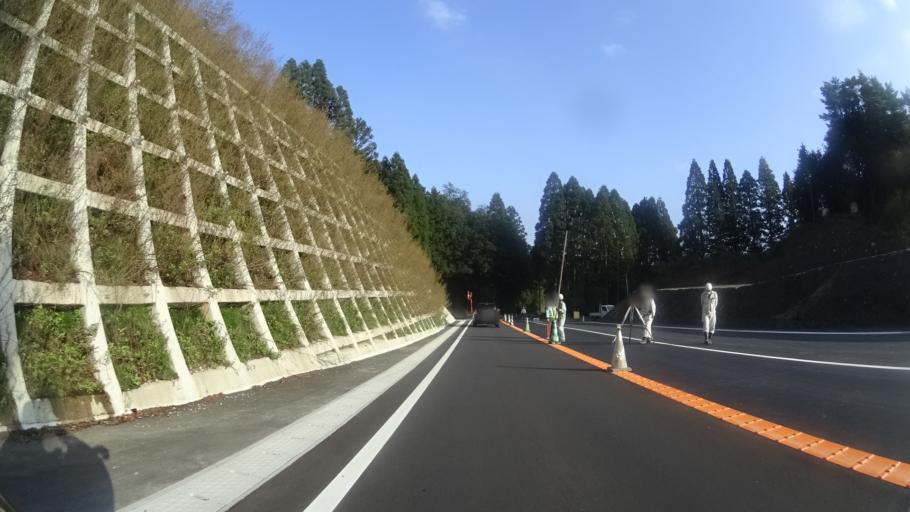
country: JP
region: Oita
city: Beppu
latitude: 33.2703
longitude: 131.4347
